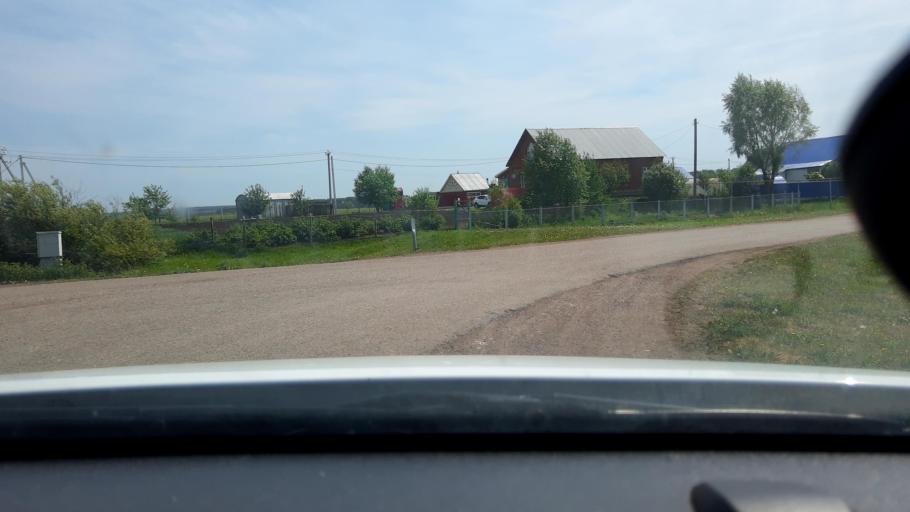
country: RU
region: Bashkortostan
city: Mikhaylovka
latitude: 54.9525
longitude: 55.7753
